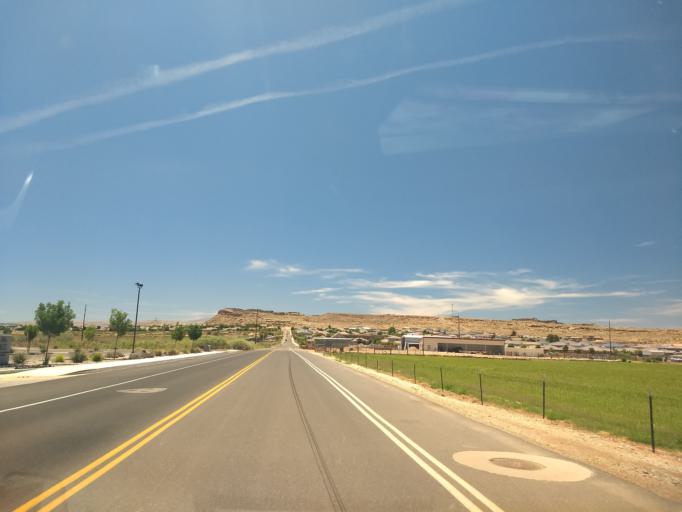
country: US
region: Utah
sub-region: Washington County
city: Washington
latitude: 37.0743
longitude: -113.5188
